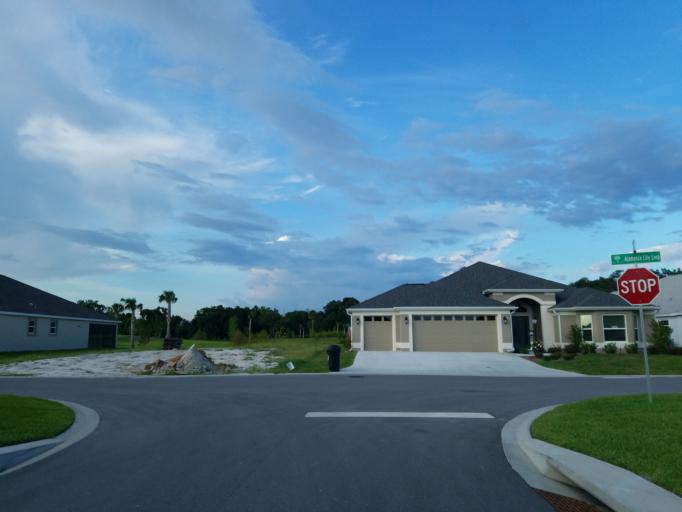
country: US
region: Florida
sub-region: Sumter County
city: Wildwood
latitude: 28.7962
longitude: -82.0222
